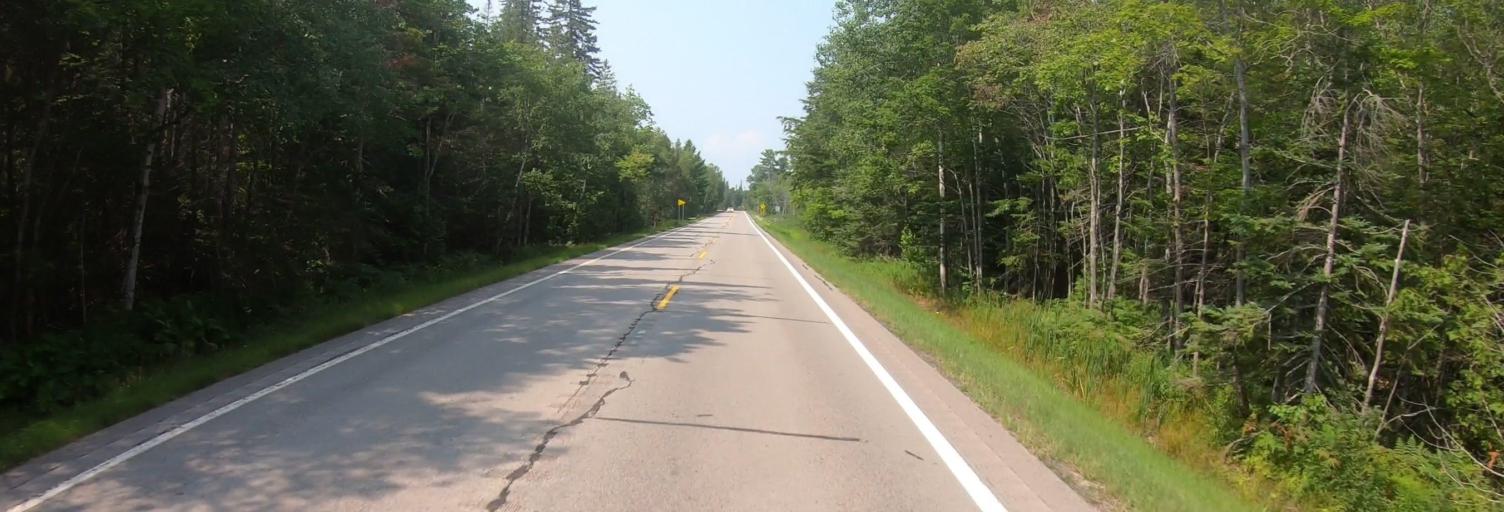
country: US
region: Michigan
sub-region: Luce County
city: Newberry
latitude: 46.5753
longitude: -85.2711
